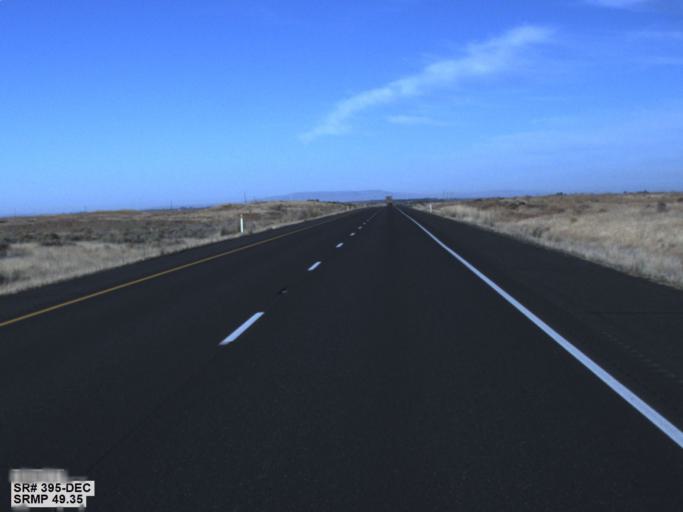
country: US
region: Washington
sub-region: Franklin County
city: Connell
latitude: 46.5988
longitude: -118.9386
